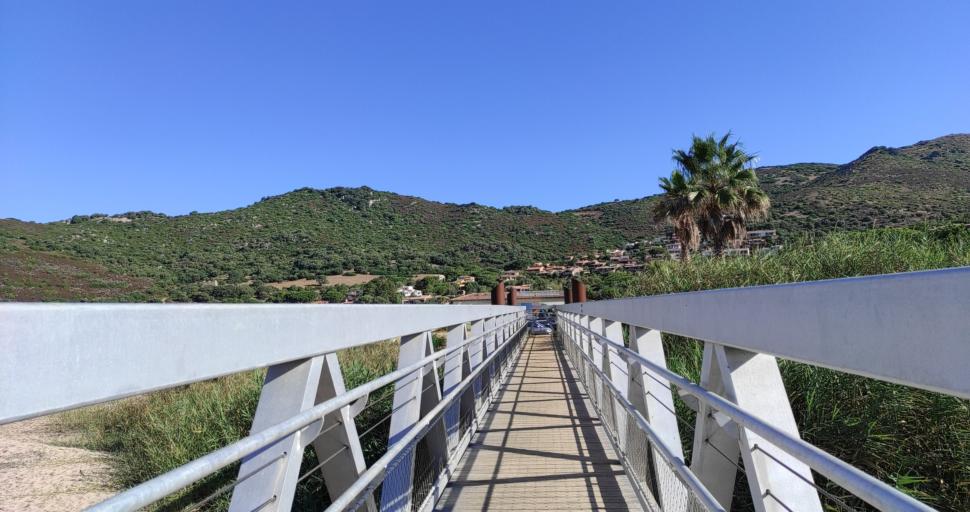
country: FR
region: Corsica
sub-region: Departement de la Corse-du-Sud
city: Alata
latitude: 41.9906
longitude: 8.6700
